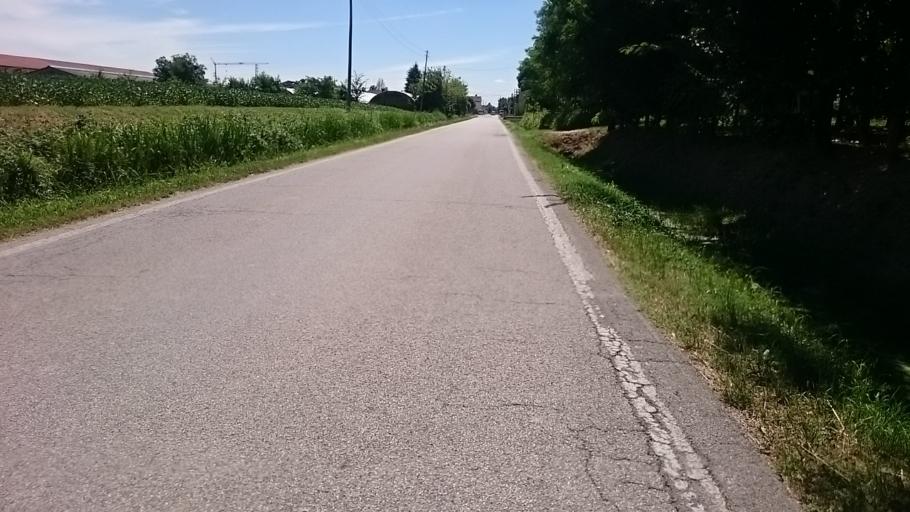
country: IT
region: Veneto
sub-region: Provincia di Padova
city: Borgoricco-San Michele delle Badesse-Sant'Eufemia
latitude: 45.5303
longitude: 11.9458
